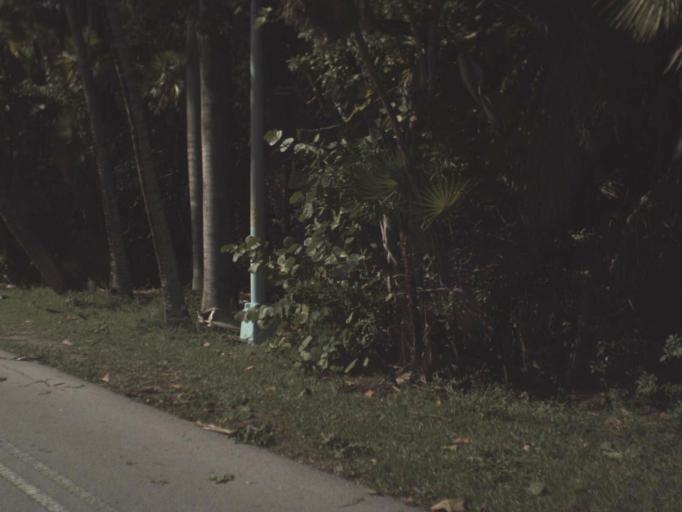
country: US
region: Florida
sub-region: Miami-Dade County
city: Key Biscayne
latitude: 25.7081
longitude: -80.1579
